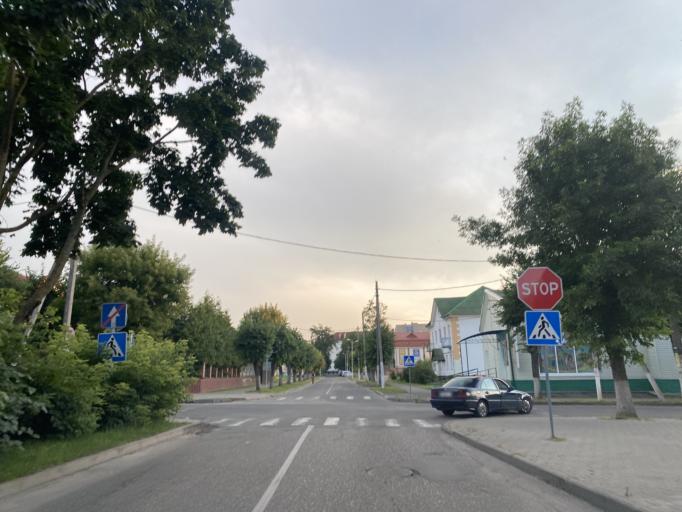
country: BY
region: Brest
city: Ivatsevichy
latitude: 52.7111
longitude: 25.3442
